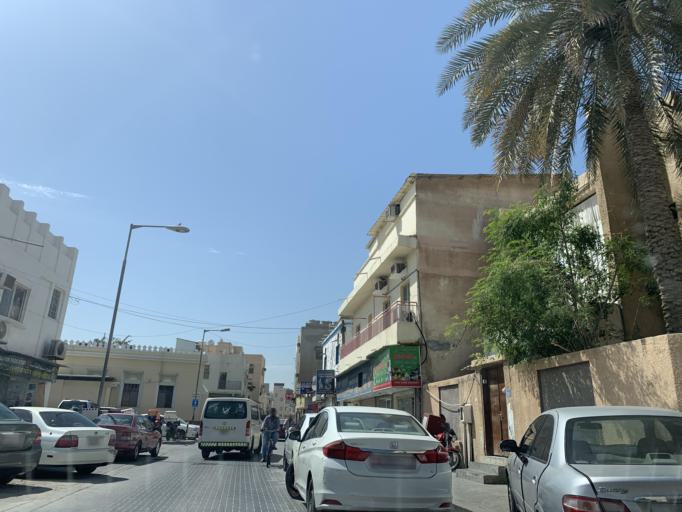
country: BH
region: Muharraq
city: Al Muharraq
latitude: 26.2570
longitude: 50.6092
